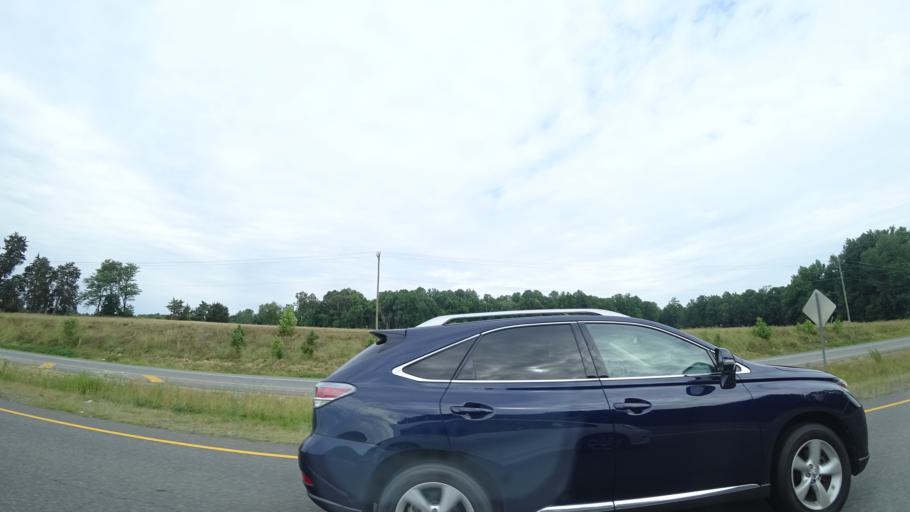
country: US
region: Virginia
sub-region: Spotsylvania County
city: Spotsylvania
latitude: 38.1867
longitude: -77.6200
